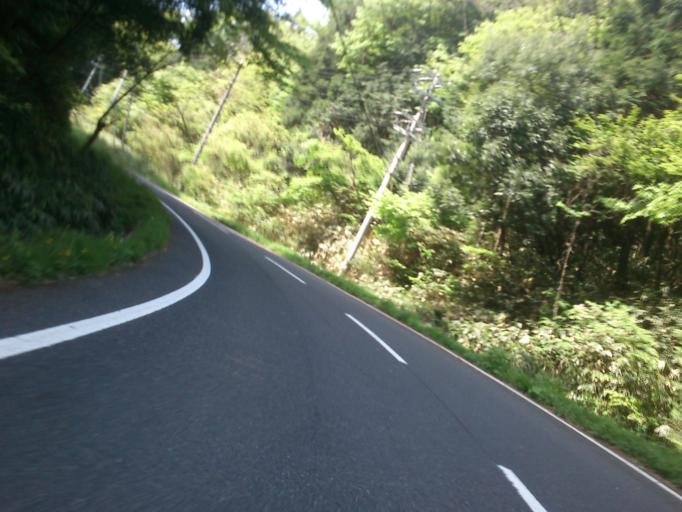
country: JP
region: Kyoto
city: Miyazu
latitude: 35.6766
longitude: 135.2482
